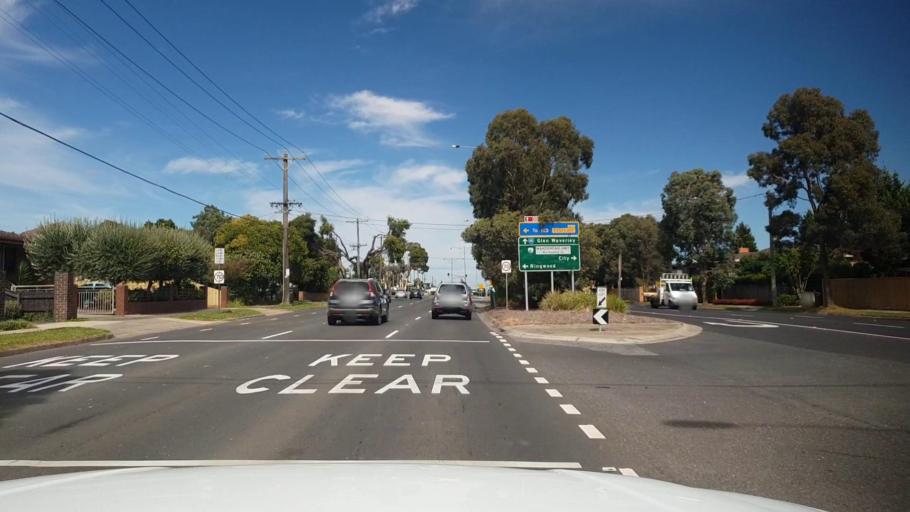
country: AU
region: Victoria
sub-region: Whitehorse
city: Nunawading
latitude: -37.8162
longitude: 145.1764
